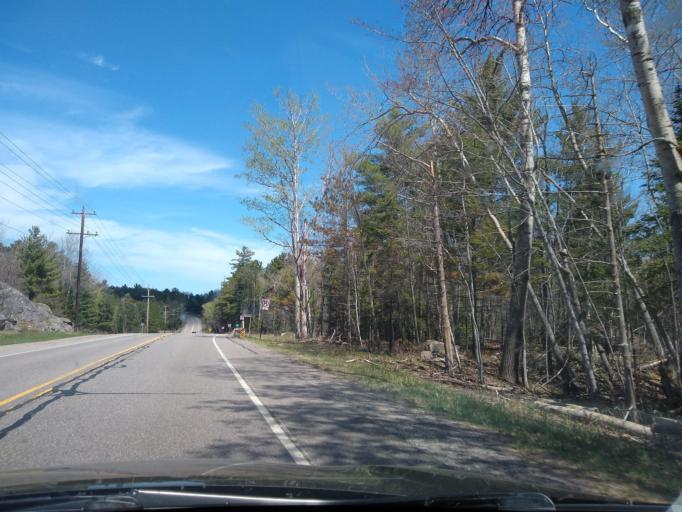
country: US
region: Michigan
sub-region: Marquette County
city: Trowbridge Park
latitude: 46.6134
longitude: -87.4699
